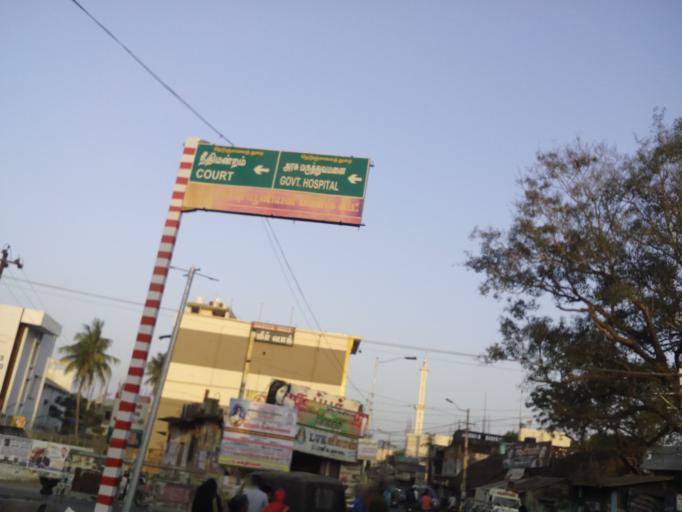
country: IN
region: Tamil Nadu
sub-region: Thanjavur
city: Kumbakonam
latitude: 10.9602
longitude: 79.3843
